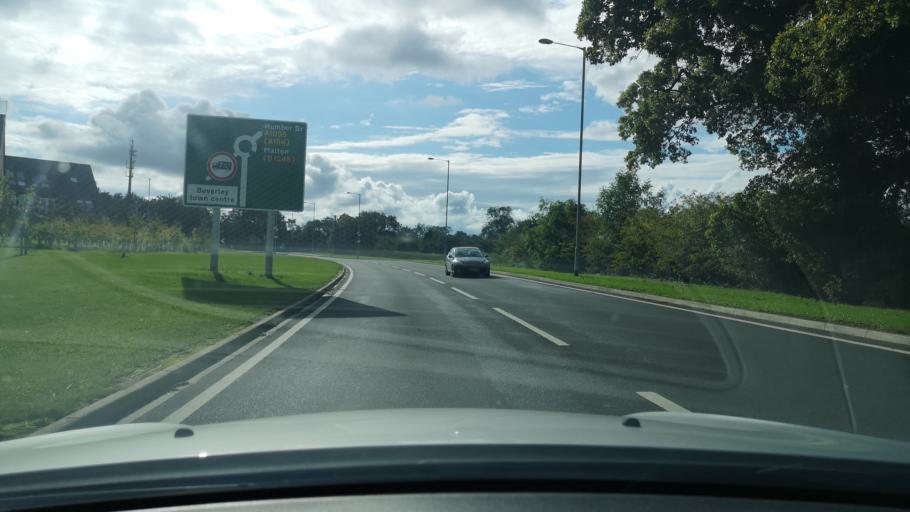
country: GB
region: England
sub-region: East Riding of Yorkshire
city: Leconfield
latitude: 53.8554
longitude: -0.4541
